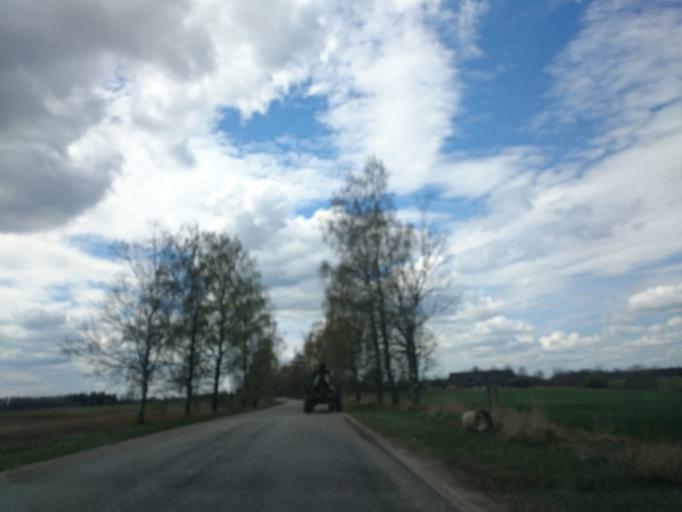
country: LV
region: Talsu Rajons
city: Sabile
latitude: 56.9509
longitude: 22.3325
